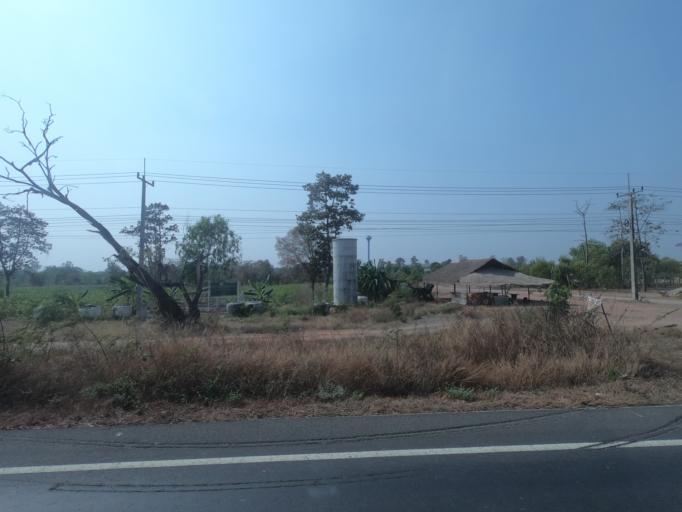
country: TH
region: Nakhon Ratchasima
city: Bua Lai
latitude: 15.6653
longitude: 102.5741
